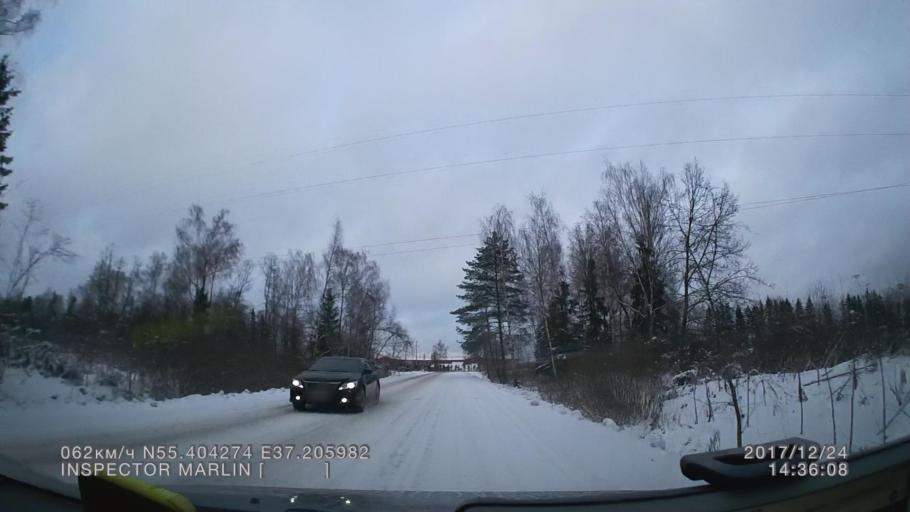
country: RU
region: Moskovskaya
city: Troitsk
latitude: 55.4043
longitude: 37.2060
